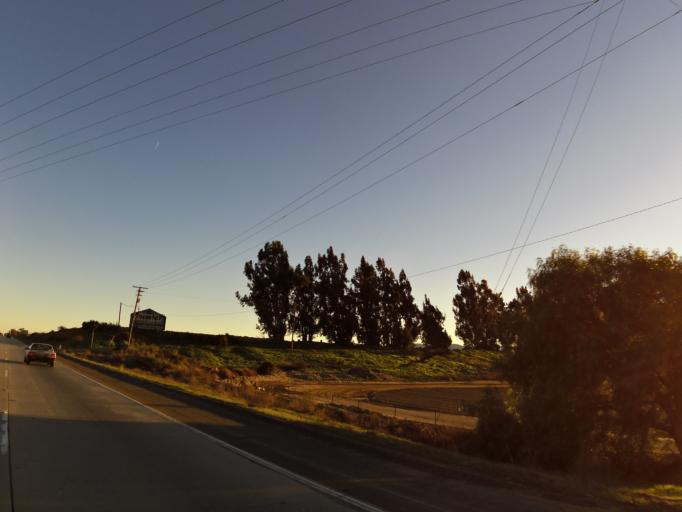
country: US
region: California
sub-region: Monterey County
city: Greenfield
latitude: 36.3490
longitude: -121.2643
